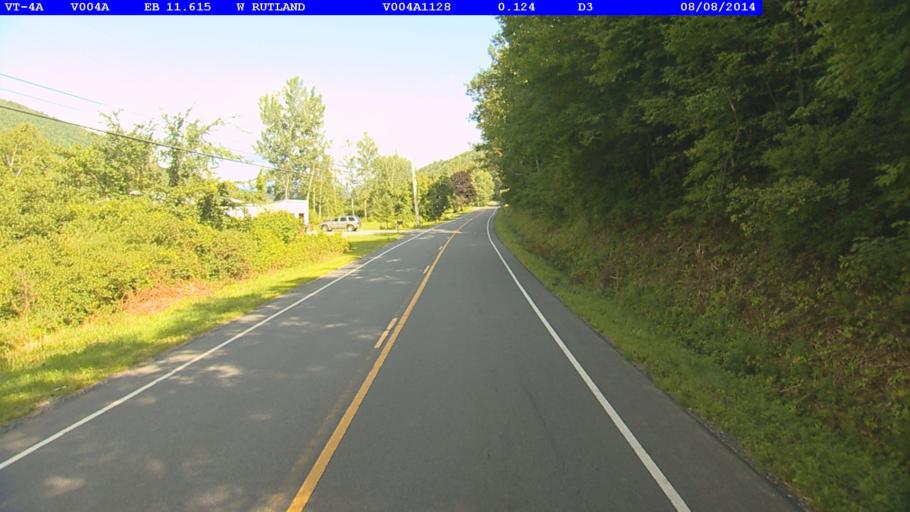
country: US
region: Vermont
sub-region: Rutland County
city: West Rutland
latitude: 43.6062
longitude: -73.0859
